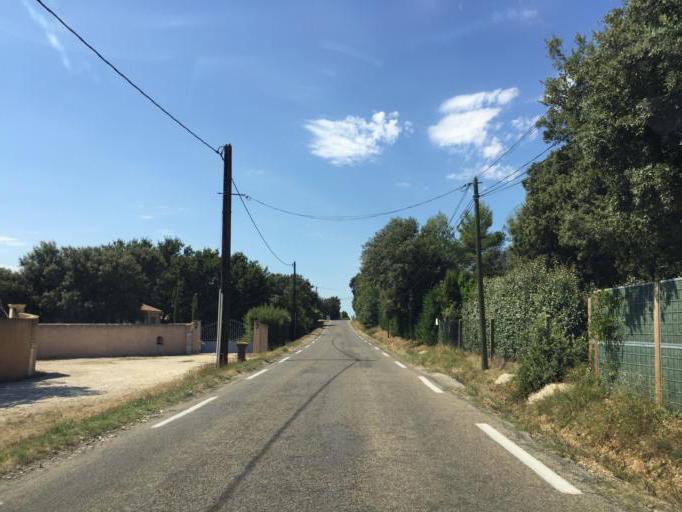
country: FR
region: Provence-Alpes-Cote d'Azur
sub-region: Departement du Vaucluse
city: Saint-Didier
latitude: 44.0175
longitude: 5.1272
